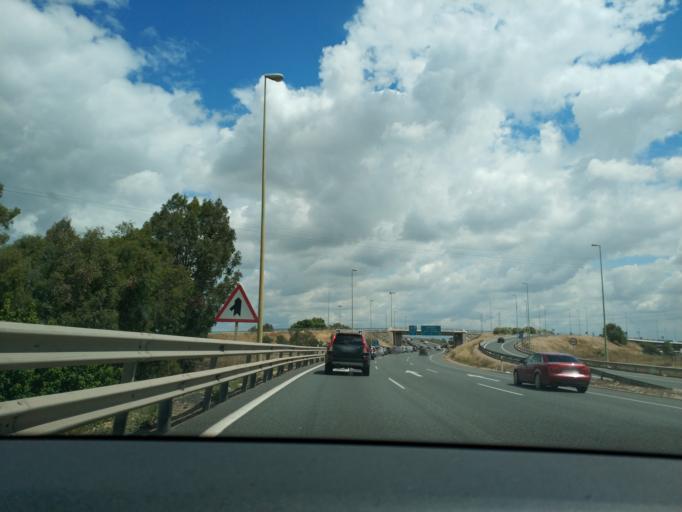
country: ES
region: Andalusia
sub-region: Provincia de Sevilla
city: Camas
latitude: 37.3860
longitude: -6.0255
